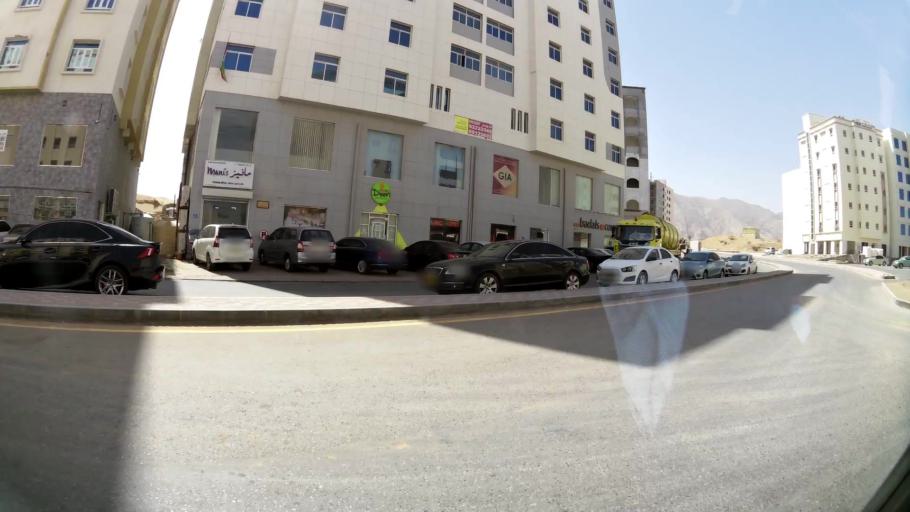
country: OM
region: Muhafazat Masqat
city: Bawshar
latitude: 23.5729
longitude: 58.4096
